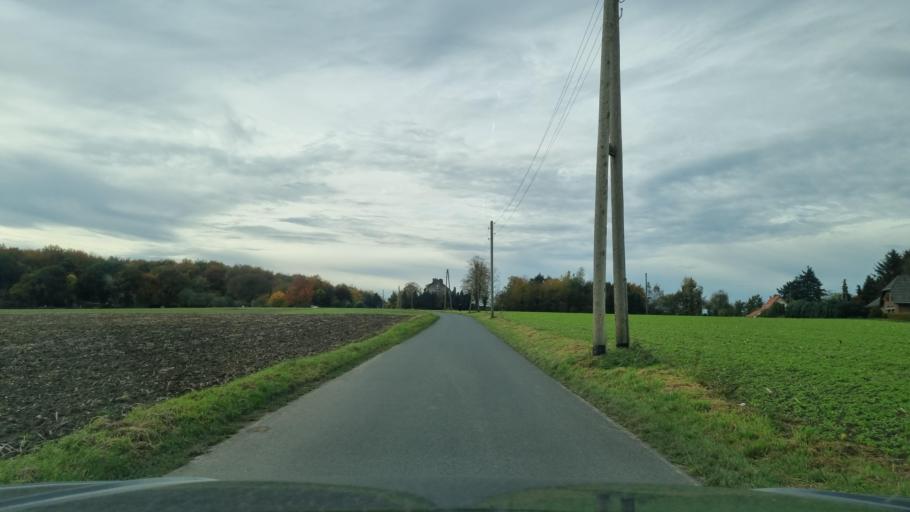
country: DE
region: North Rhine-Westphalia
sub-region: Regierungsbezirk Dusseldorf
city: Kranenburg
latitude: 51.7752
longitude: 6.0164
